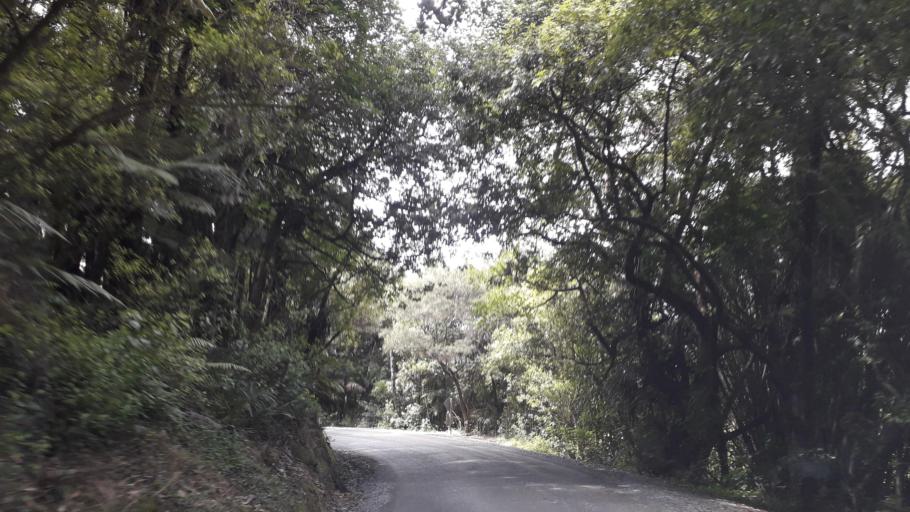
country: NZ
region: Northland
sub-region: Far North District
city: Kaitaia
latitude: -35.1707
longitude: 173.3345
